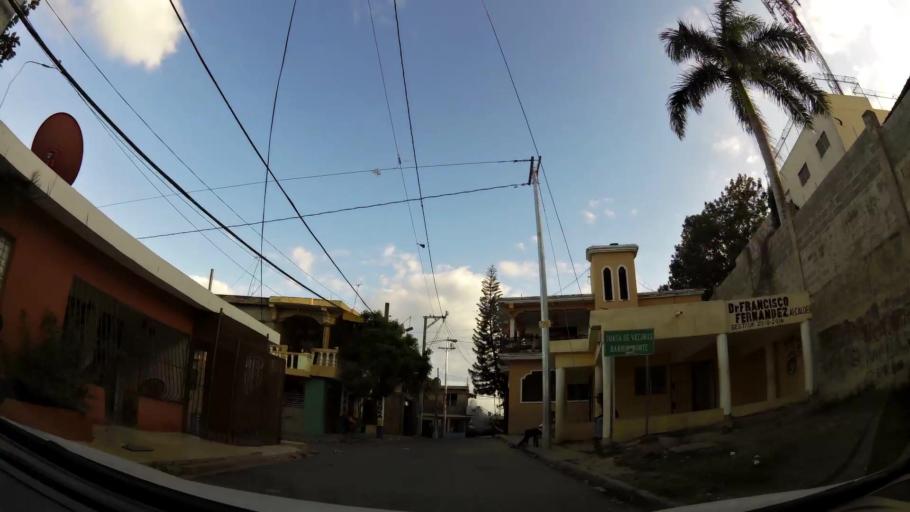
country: DO
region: Nacional
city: La Agustina
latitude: 18.5454
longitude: -69.9242
